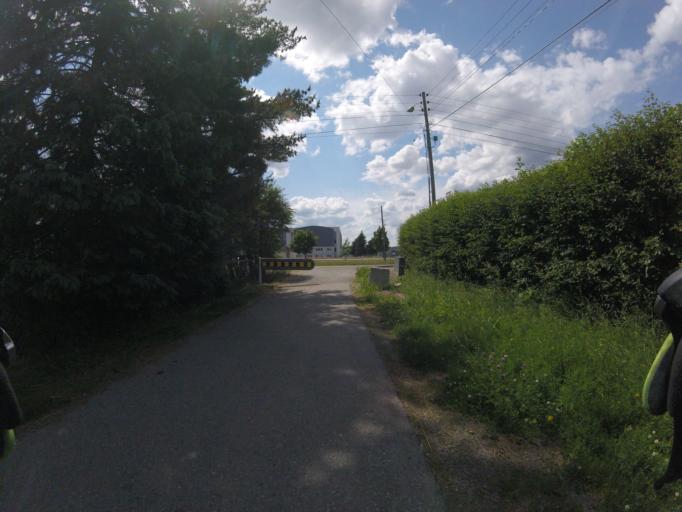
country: NO
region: Akershus
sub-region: Skedsmo
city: Lillestrom
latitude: 59.9723
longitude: 11.0450
